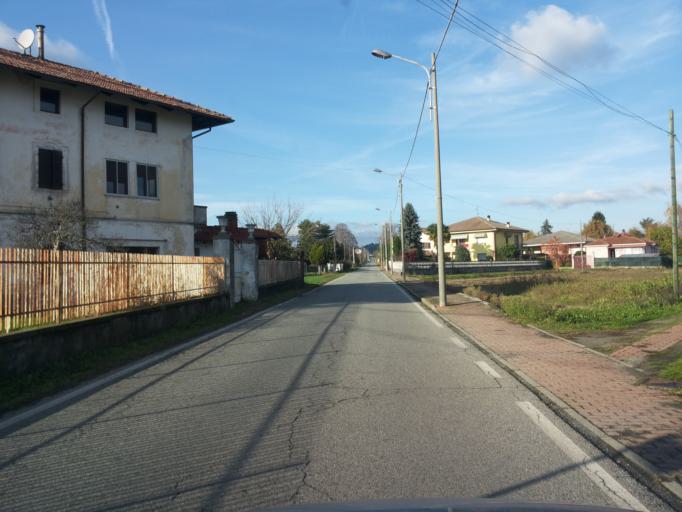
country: IT
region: Piedmont
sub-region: Provincia di Vercelli
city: Alice Castello
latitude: 45.3713
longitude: 8.0747
